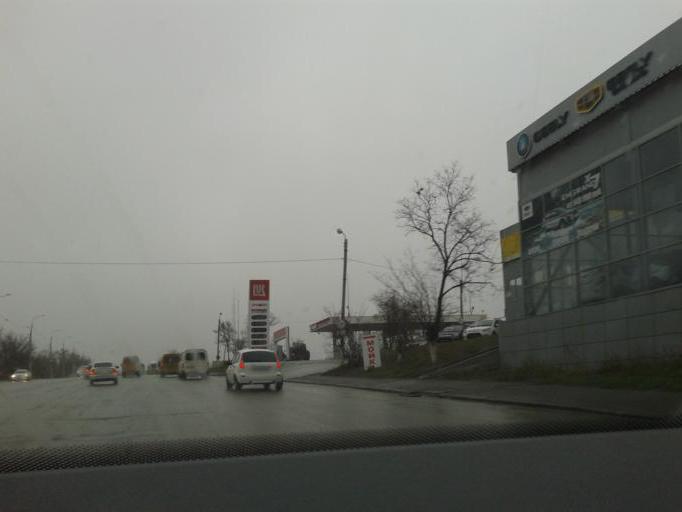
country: RU
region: Volgograd
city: Volgograd
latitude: 48.6685
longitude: 44.4416
